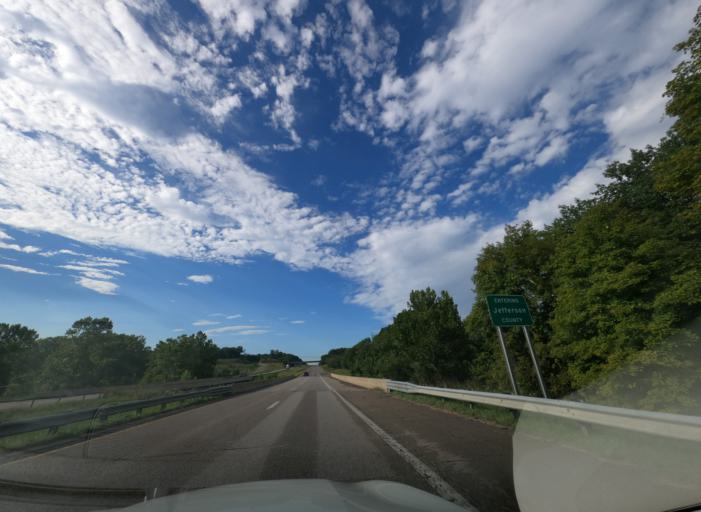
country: US
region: Missouri
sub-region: Jefferson County
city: Crystal City
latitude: 38.0889
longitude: -90.2991
